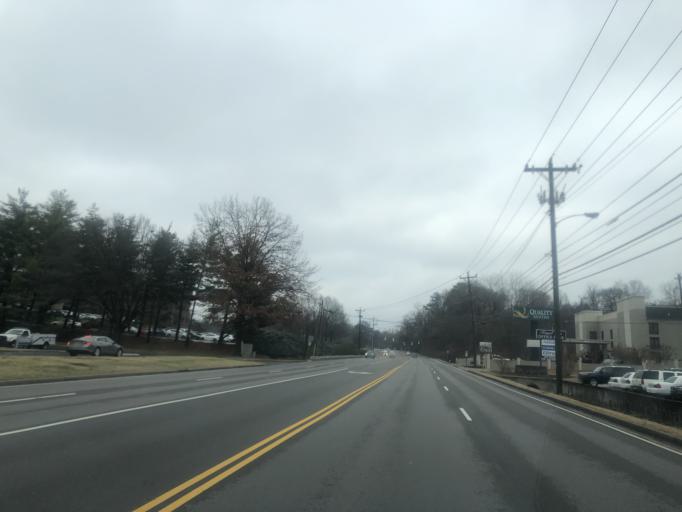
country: US
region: Tennessee
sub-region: Davidson County
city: Lakewood
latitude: 36.1516
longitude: -86.6768
